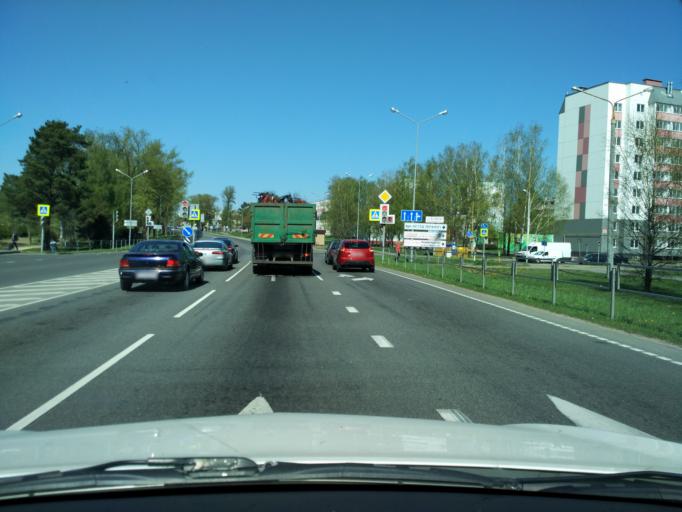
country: BY
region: Minsk
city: Borovlyany
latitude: 53.9919
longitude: 27.6698
